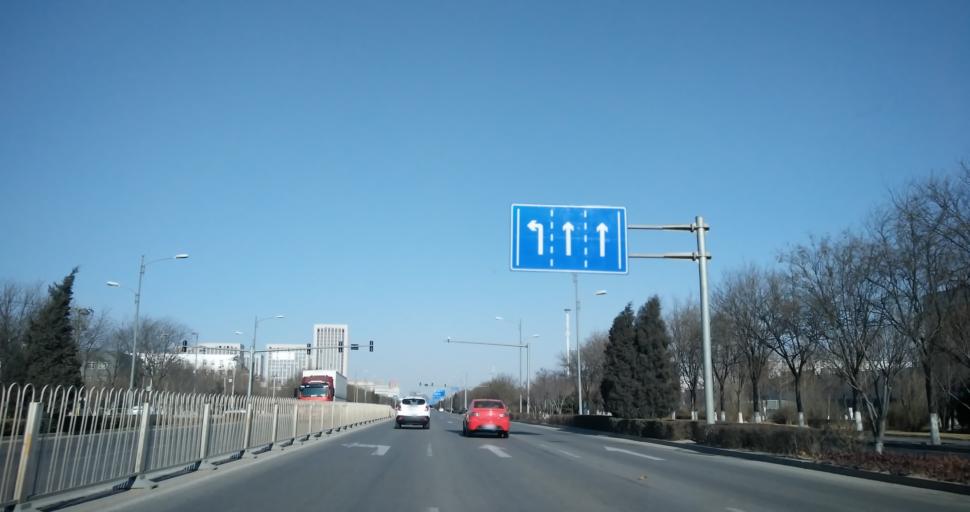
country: CN
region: Beijing
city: Yinghai
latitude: 39.7420
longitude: 116.4969
